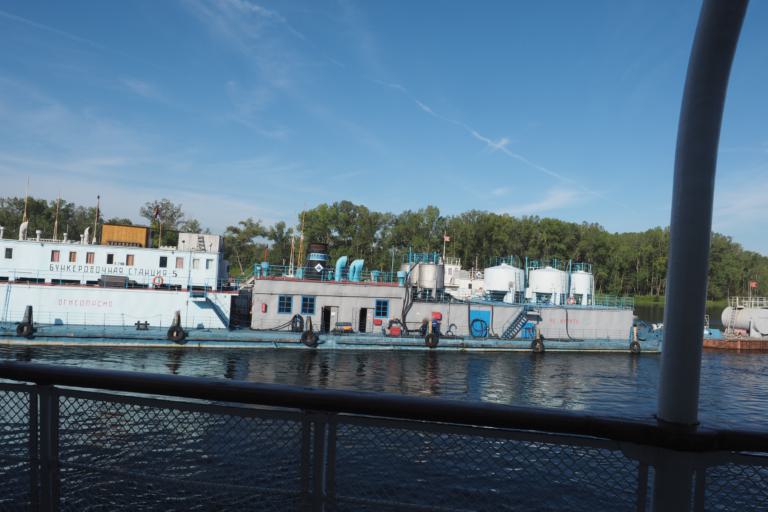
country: RU
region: Krasnoyarskiy
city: Berezovka
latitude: 56.1395
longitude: 93.1332
